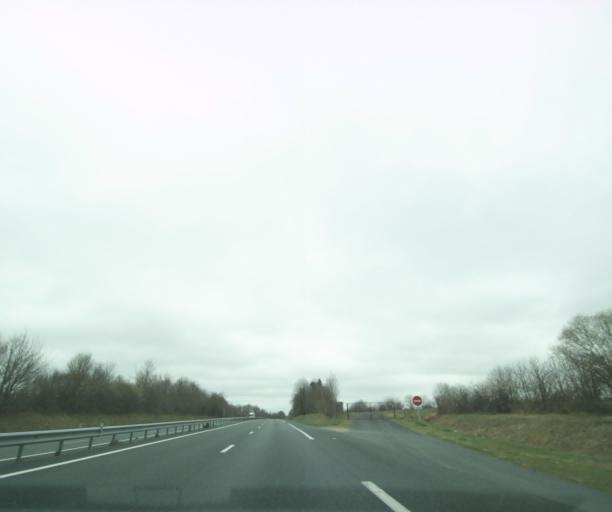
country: FR
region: Centre
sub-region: Departement de l'Indre
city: Chantome
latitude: 46.4236
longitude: 1.4722
